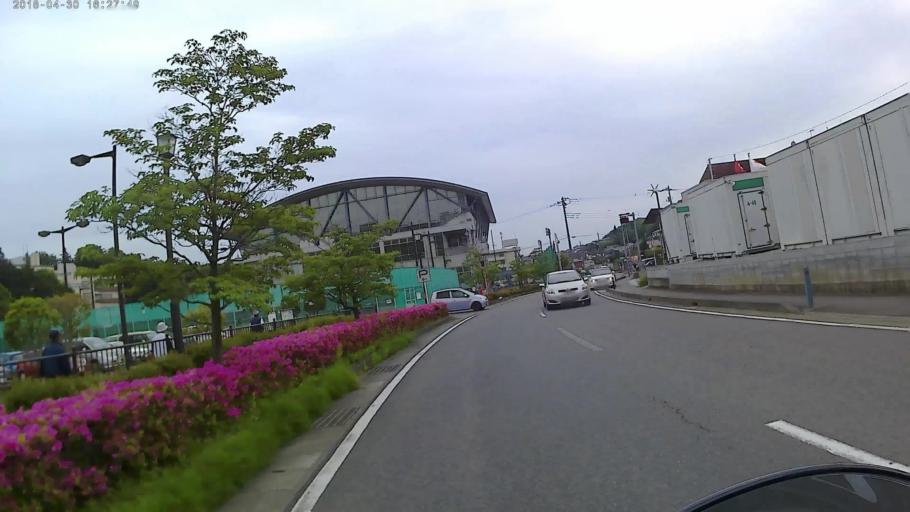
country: JP
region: Kanagawa
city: Zama
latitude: 35.4663
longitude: 139.4100
